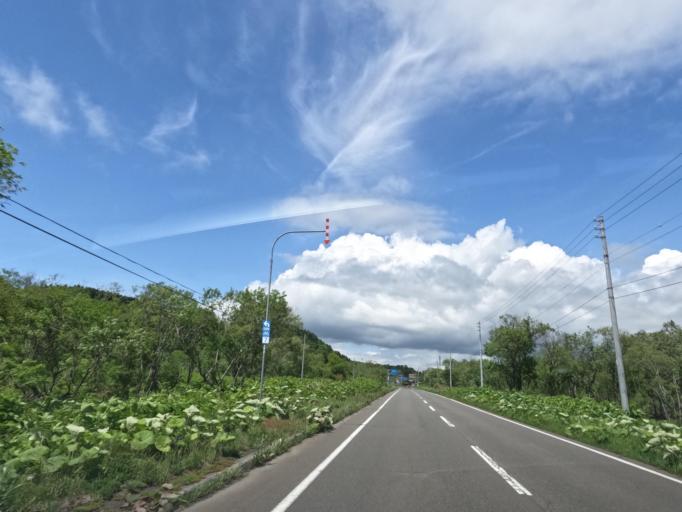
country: JP
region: Hokkaido
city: Tobetsu
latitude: 43.3949
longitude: 141.5799
